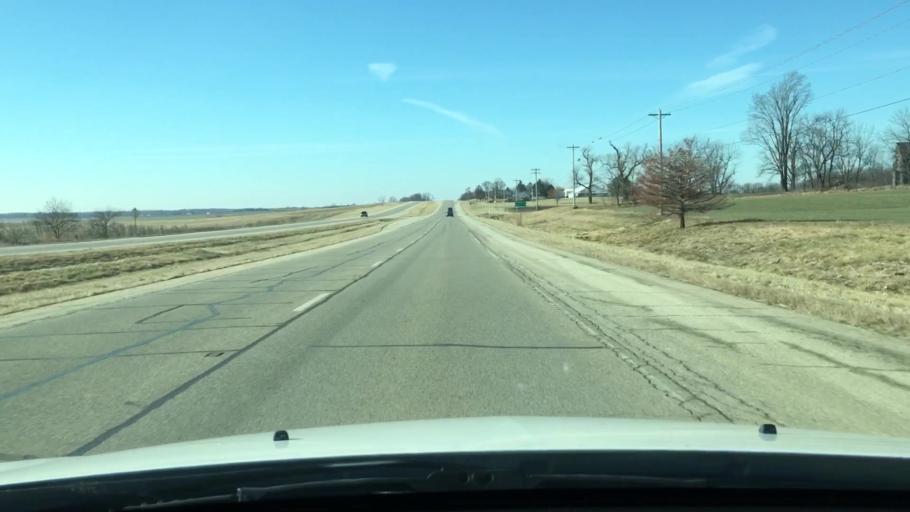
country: US
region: Illinois
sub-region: Woodford County
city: Metamora
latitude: 40.7840
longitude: -89.3907
